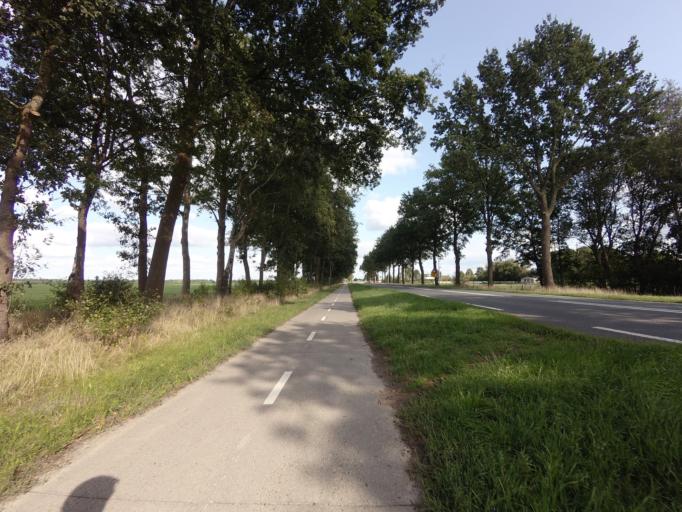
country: NL
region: Drenthe
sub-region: Gemeente Westerveld
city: Dwingeloo
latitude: 52.8392
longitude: 6.3709
